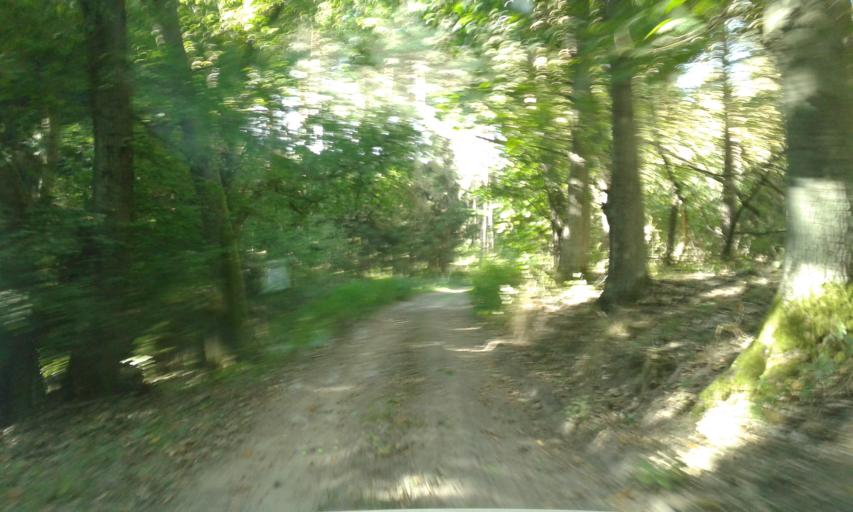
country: PL
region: West Pomeranian Voivodeship
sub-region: Powiat stargardzki
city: Dolice
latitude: 53.2367
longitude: 15.2588
